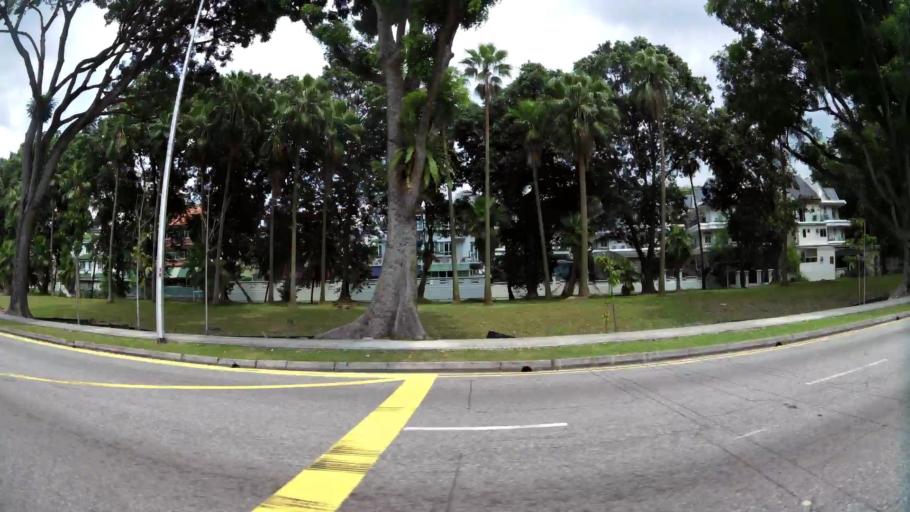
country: SG
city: Singapore
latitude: 1.2848
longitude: 103.7801
